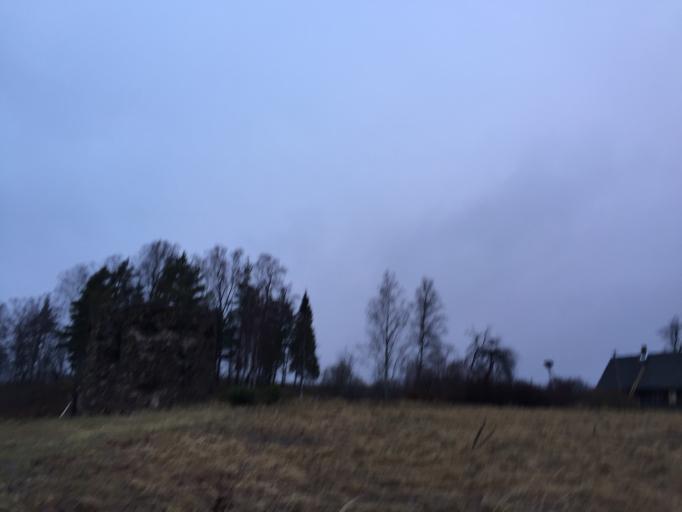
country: LV
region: Pargaujas
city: Stalbe
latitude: 57.4176
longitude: 24.9799
